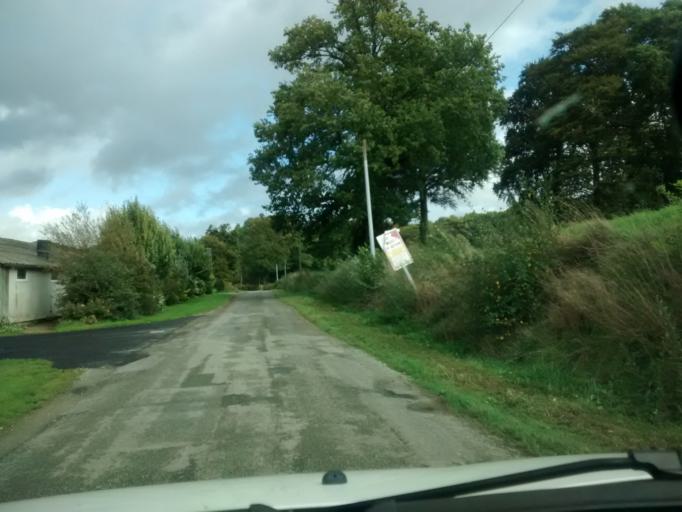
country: FR
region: Brittany
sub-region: Departement d'Ille-et-Vilaine
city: Chateaubourg
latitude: 48.1364
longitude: -1.4179
